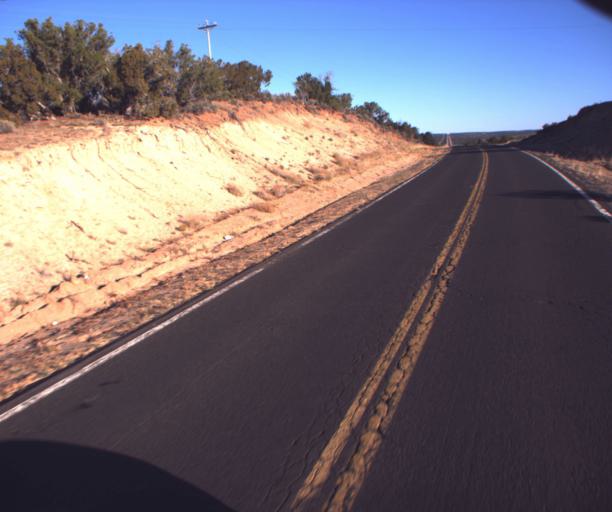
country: US
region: Arizona
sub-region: Apache County
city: Ganado
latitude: 35.5175
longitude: -109.5261
